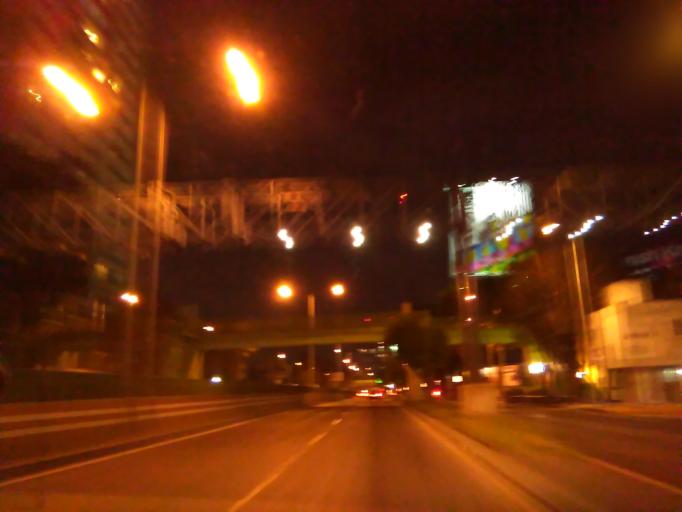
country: MX
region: Mexico City
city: Miguel Hidalgo
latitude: 19.4454
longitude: -99.2016
